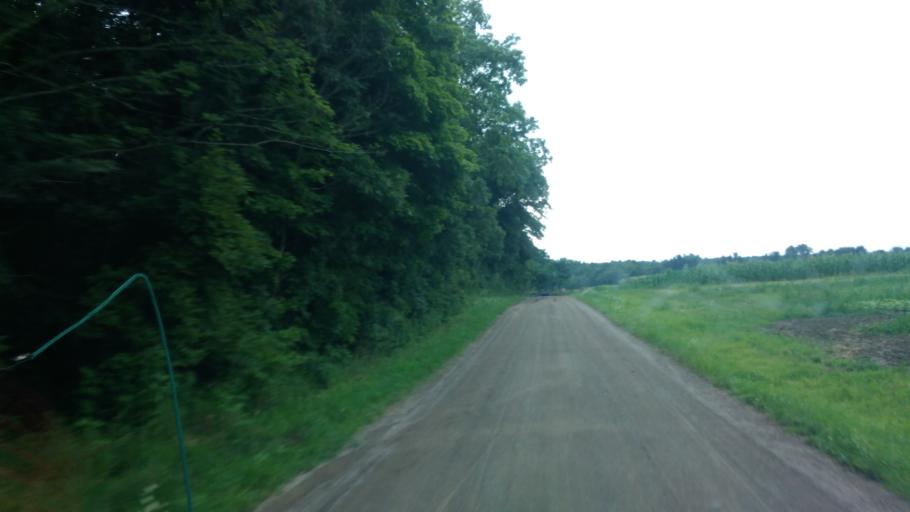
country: US
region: Ohio
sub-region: Knox County
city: Gambier
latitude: 40.2929
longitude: -82.3120
